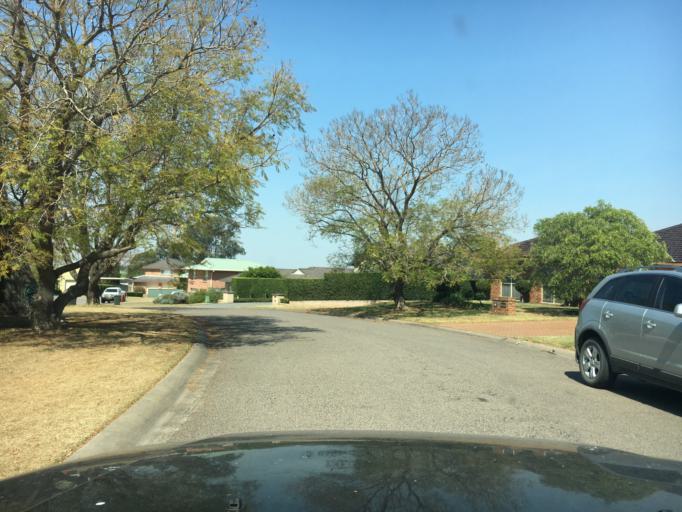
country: AU
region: New South Wales
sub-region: Singleton
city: Singleton
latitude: -32.5745
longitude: 151.1859
